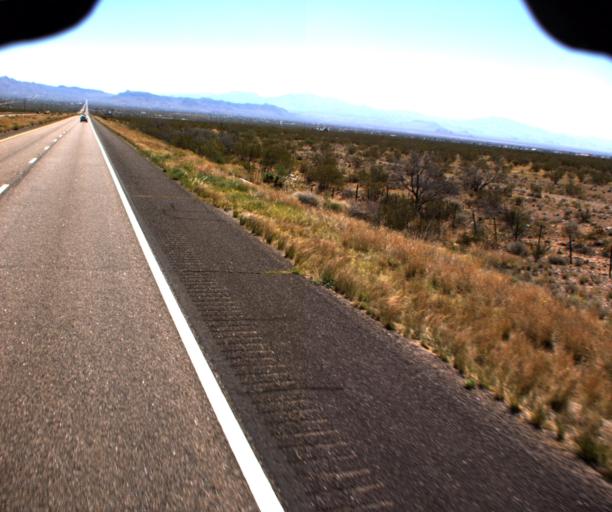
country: US
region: Arizona
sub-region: Mohave County
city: Golden Valley
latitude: 35.2268
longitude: -114.3178
